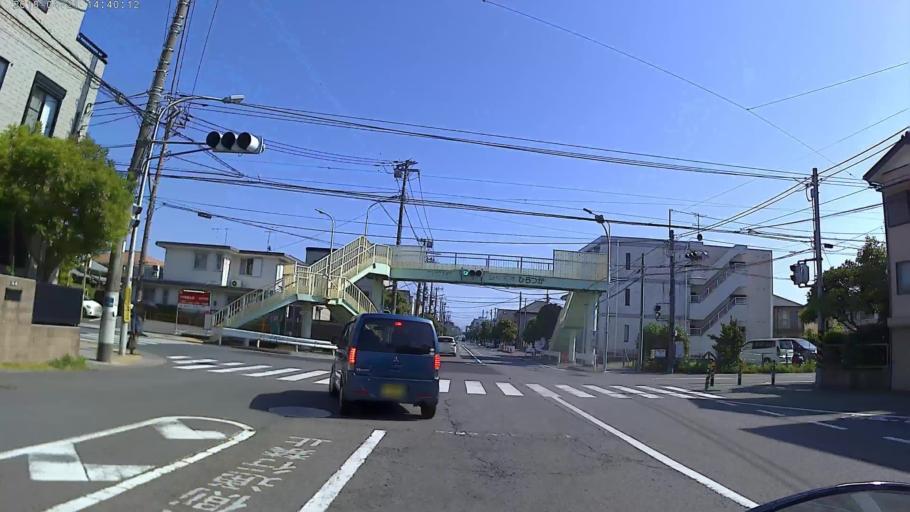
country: JP
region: Kanagawa
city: Hiratsuka
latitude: 35.3254
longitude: 139.3461
